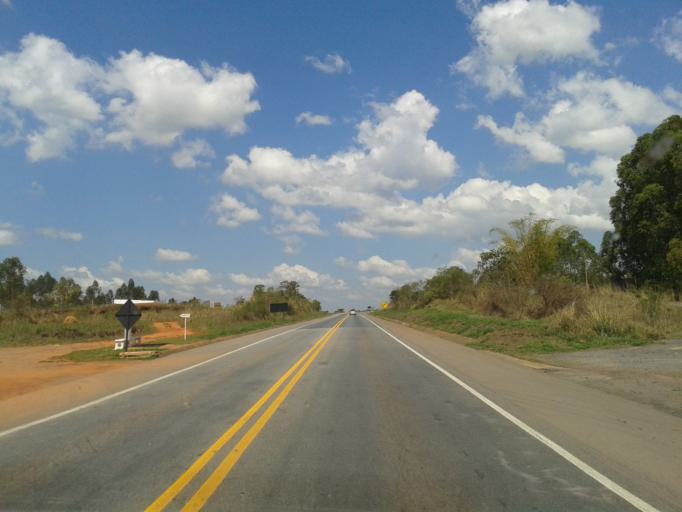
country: BR
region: Minas Gerais
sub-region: Campos Altos
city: Campos Altos
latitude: -19.6818
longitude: -46.0418
